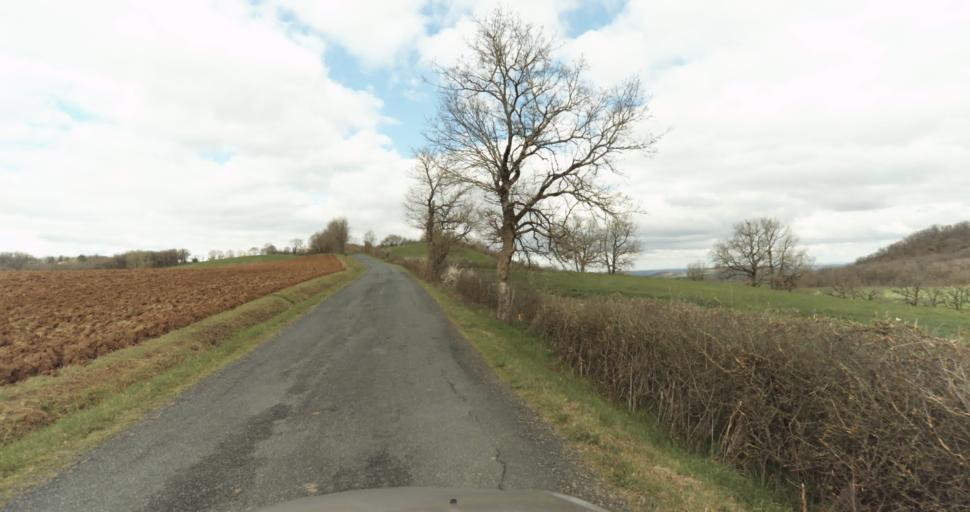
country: FR
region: Midi-Pyrenees
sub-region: Departement du Tarn
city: Frejairolles
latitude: 43.8646
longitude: 2.2168
